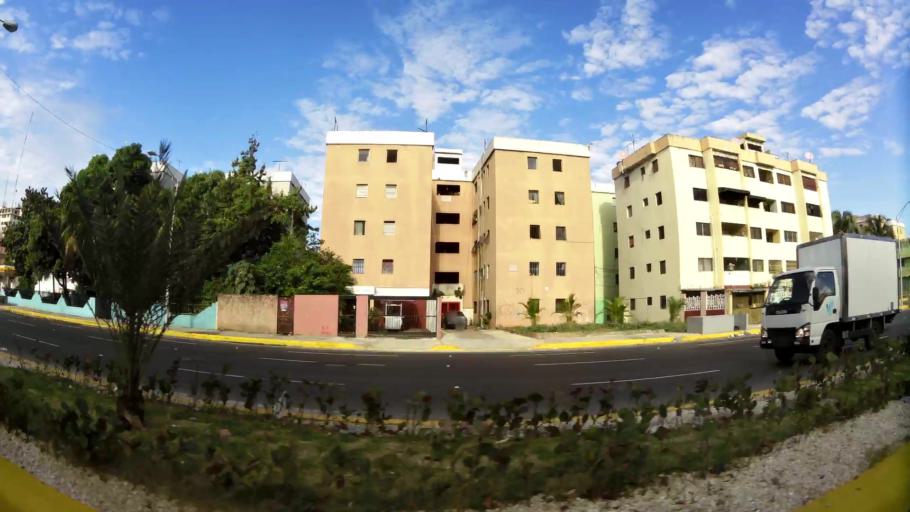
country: DO
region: Nacional
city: San Carlos
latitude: 18.4848
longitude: -69.9044
